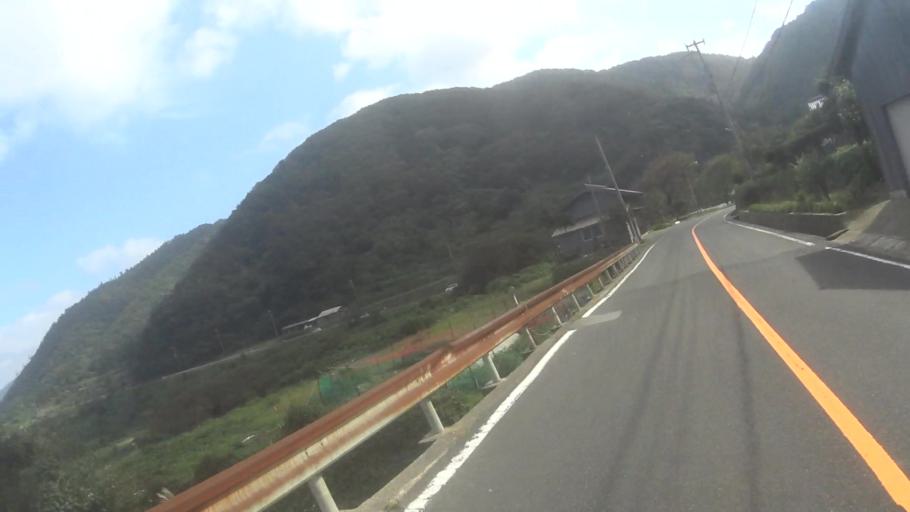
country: JP
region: Kyoto
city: Miyazu
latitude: 35.7490
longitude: 135.1438
